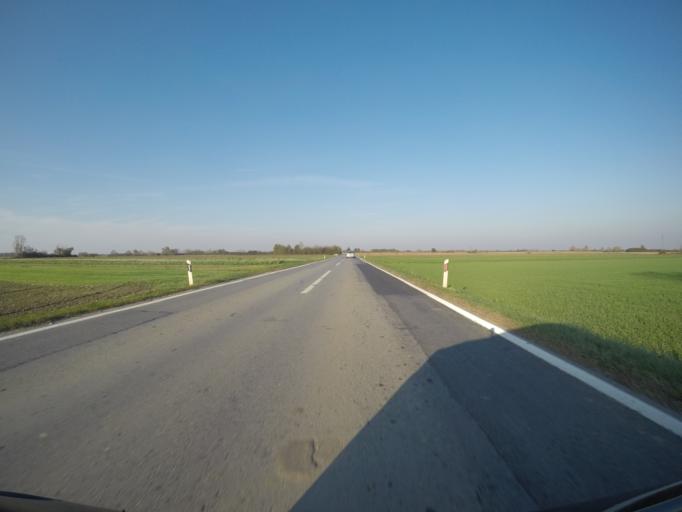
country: HU
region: Somogy
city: Barcs
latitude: 45.9169
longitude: 17.4488
